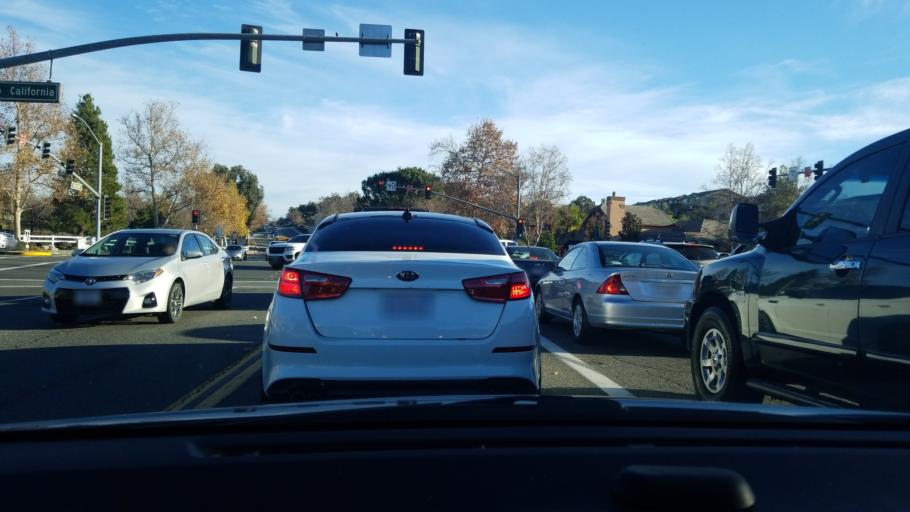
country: US
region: California
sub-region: Riverside County
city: Temecula
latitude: 33.5032
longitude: -117.1488
